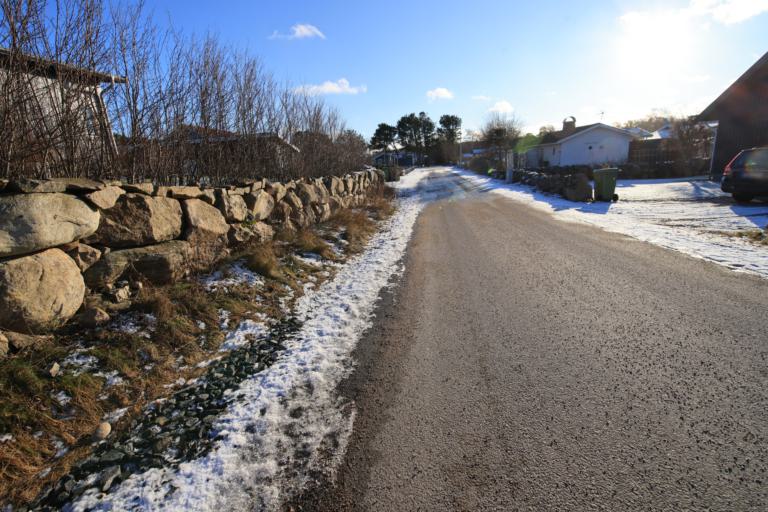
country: SE
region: Halland
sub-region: Varbergs Kommun
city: Traslovslage
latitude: 57.0654
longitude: 12.2862
